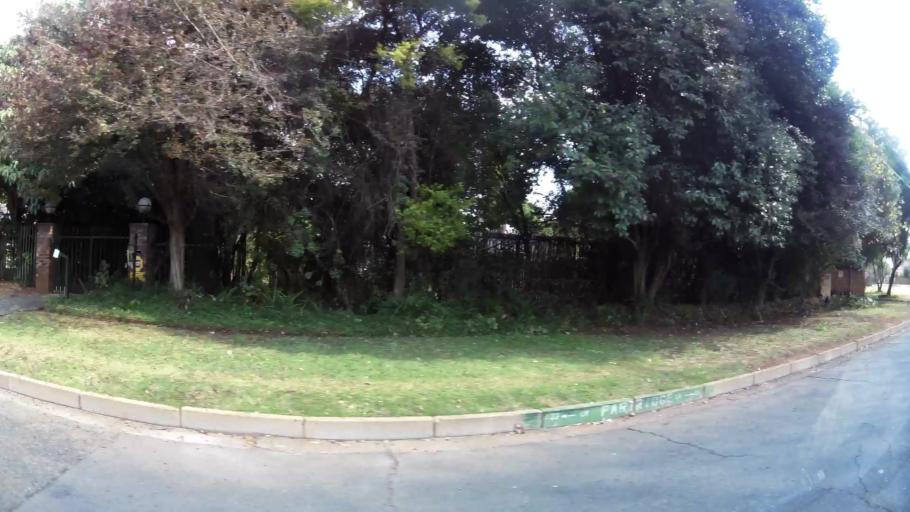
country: ZA
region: Gauteng
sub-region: City of Johannesburg Metropolitan Municipality
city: Modderfontein
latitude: -26.0843
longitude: 28.2346
